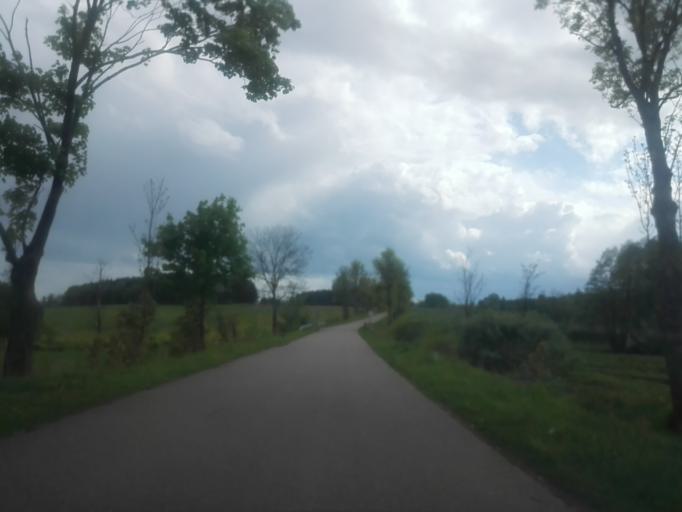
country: PL
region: Podlasie
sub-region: Powiat lomzynski
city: Wizna
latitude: 53.2708
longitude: 22.4527
